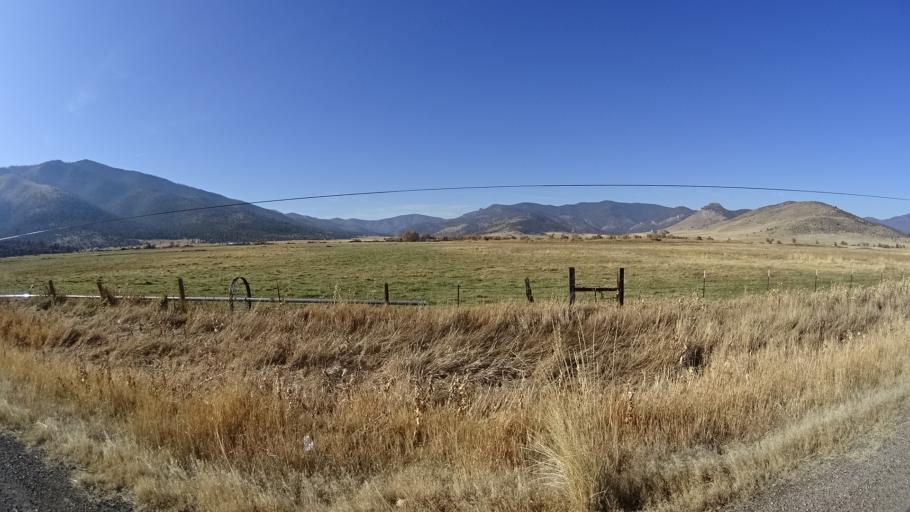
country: US
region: California
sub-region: Siskiyou County
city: Weed
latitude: 41.5028
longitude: -122.5153
